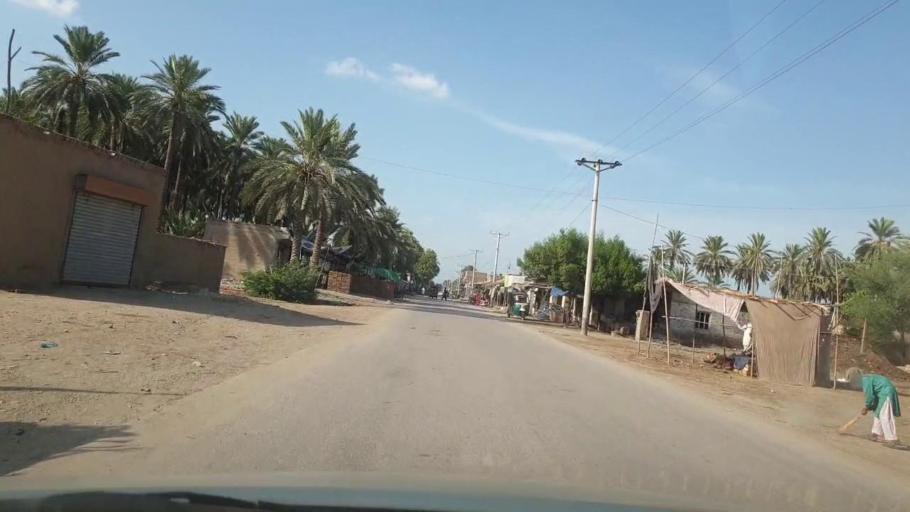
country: PK
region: Sindh
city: Sukkur
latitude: 27.6557
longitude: 68.8404
